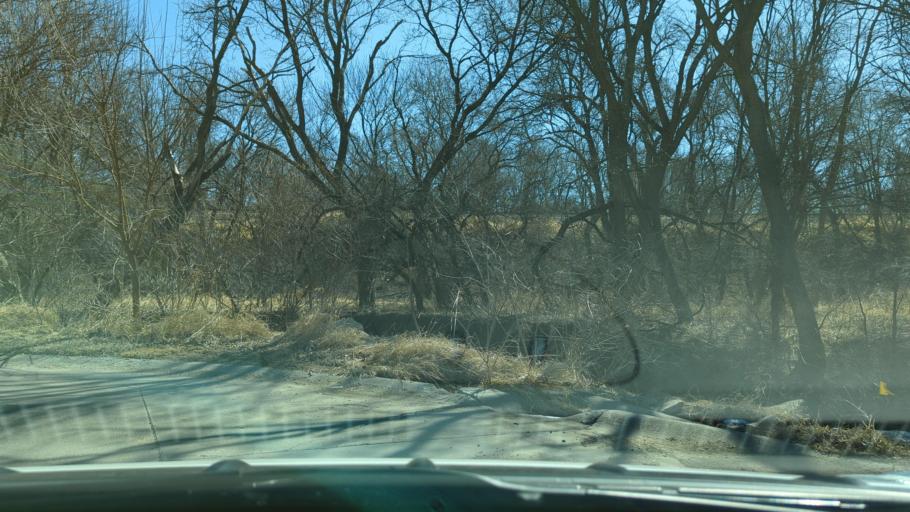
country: US
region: Nebraska
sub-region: Douglas County
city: Ralston
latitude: 41.1836
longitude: -96.0700
